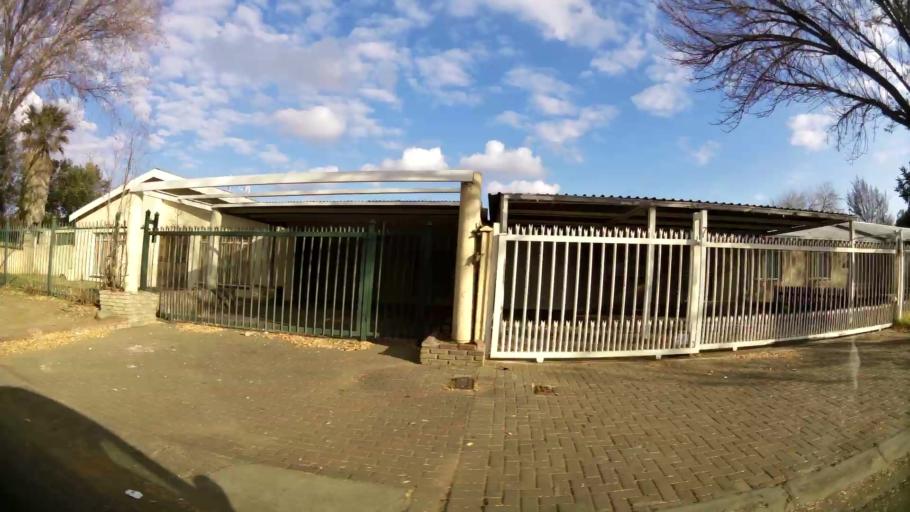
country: ZA
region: Orange Free State
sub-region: Mangaung Metropolitan Municipality
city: Bloemfontein
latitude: -29.0990
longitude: 26.1906
